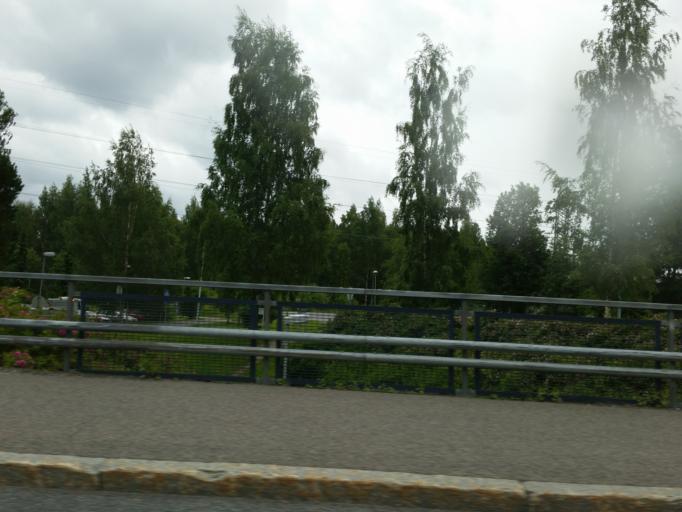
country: FI
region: Northern Savo
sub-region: Kuopio
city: Kuopio
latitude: 62.8904
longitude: 27.6347
